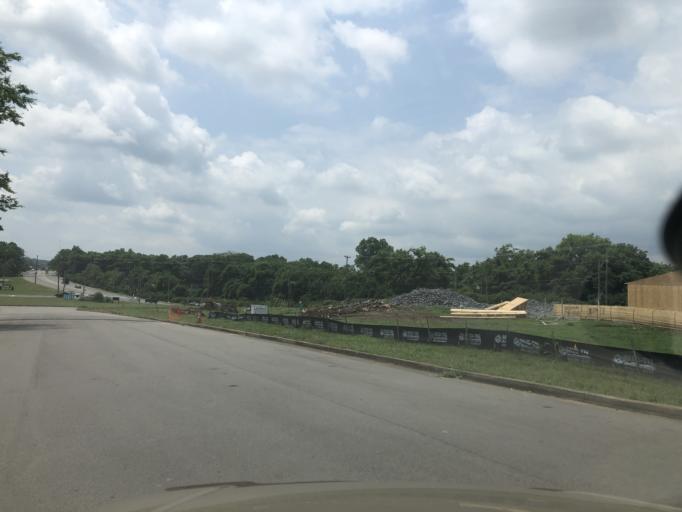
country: US
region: Tennessee
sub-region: Davidson County
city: Lakewood
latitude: 36.2343
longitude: -86.6241
